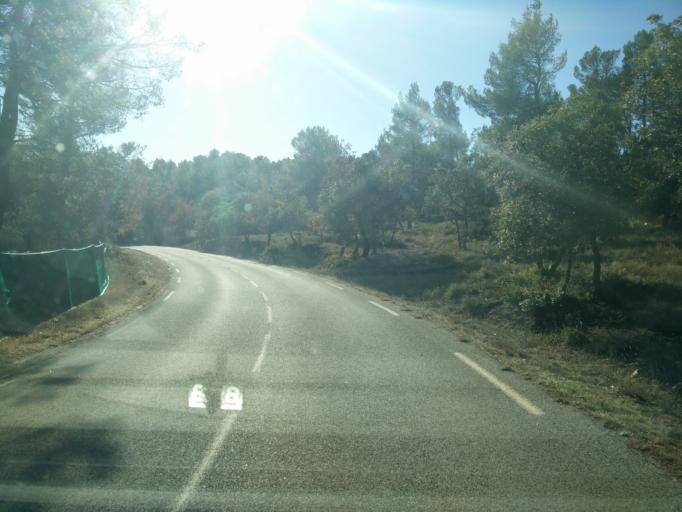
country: FR
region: Provence-Alpes-Cote d'Azur
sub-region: Departement du Var
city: Aups
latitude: 43.5960
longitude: 6.2206
